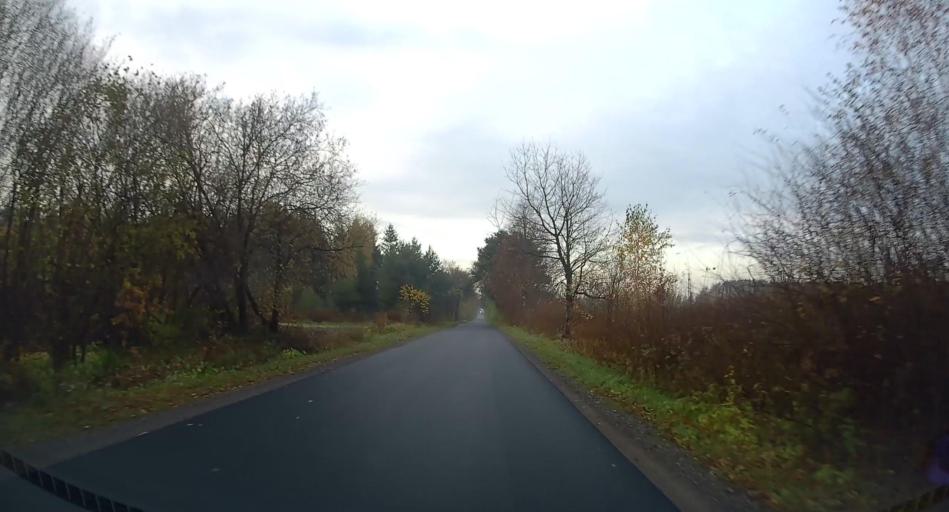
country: PL
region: Masovian Voivodeship
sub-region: Powiat zyrardowski
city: Puszcza Marianska
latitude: 51.9359
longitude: 20.3653
